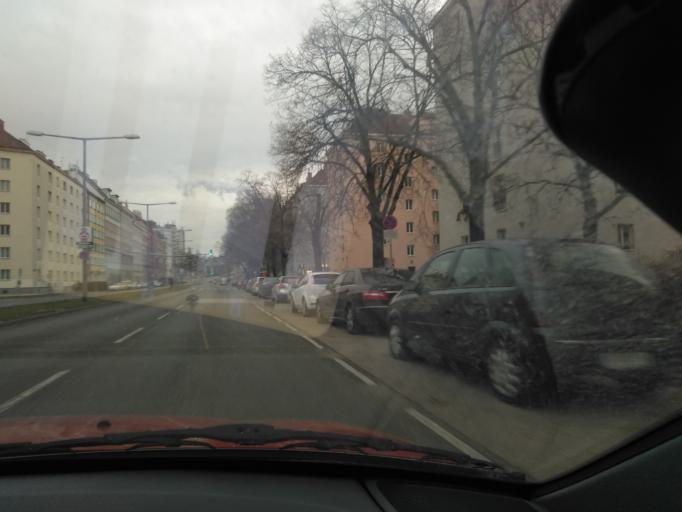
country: AT
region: Vienna
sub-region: Wien Stadt
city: Vienna
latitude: 48.2389
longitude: 16.3680
